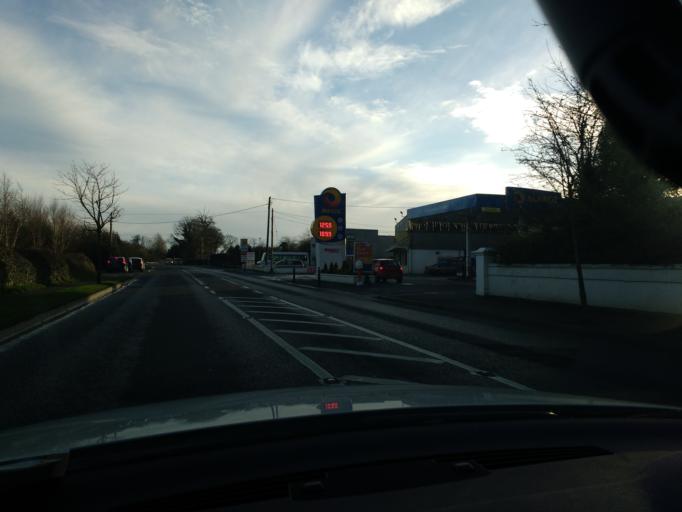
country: IE
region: Munster
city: Thurles
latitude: 52.6667
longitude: -7.8068
